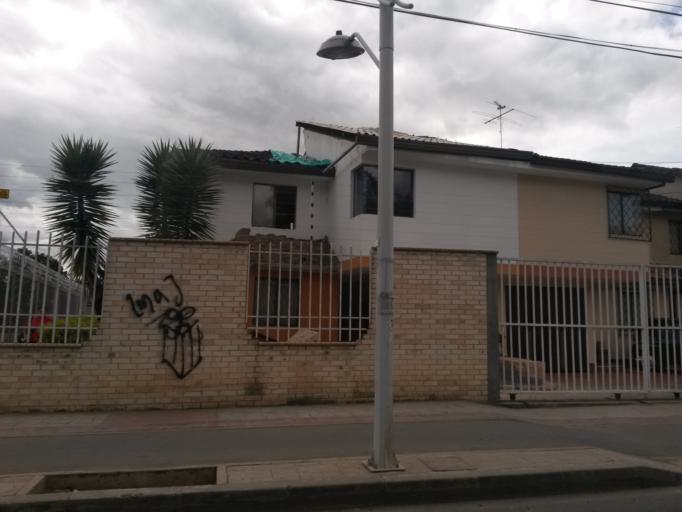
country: CO
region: Cauca
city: Popayan
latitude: 2.4481
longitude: -76.5952
